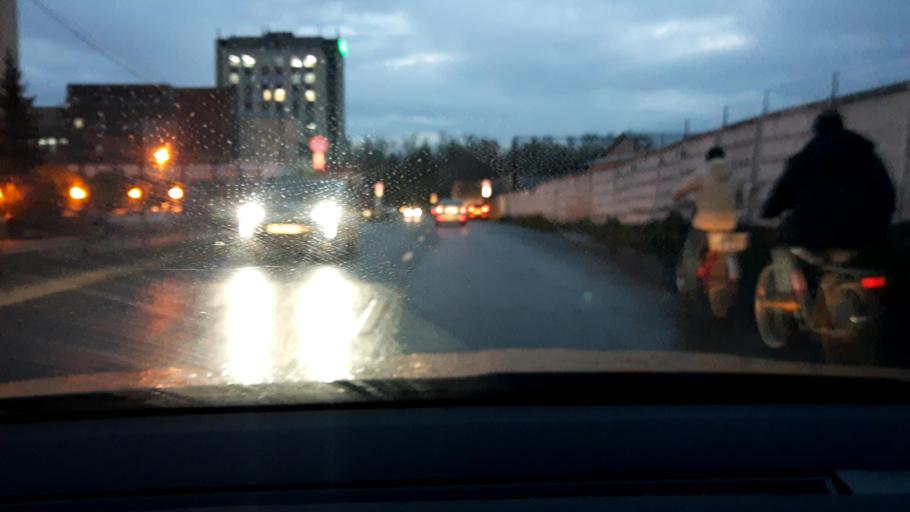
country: RU
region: Moscow
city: Kuz'minki
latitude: 55.7088
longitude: 37.8024
